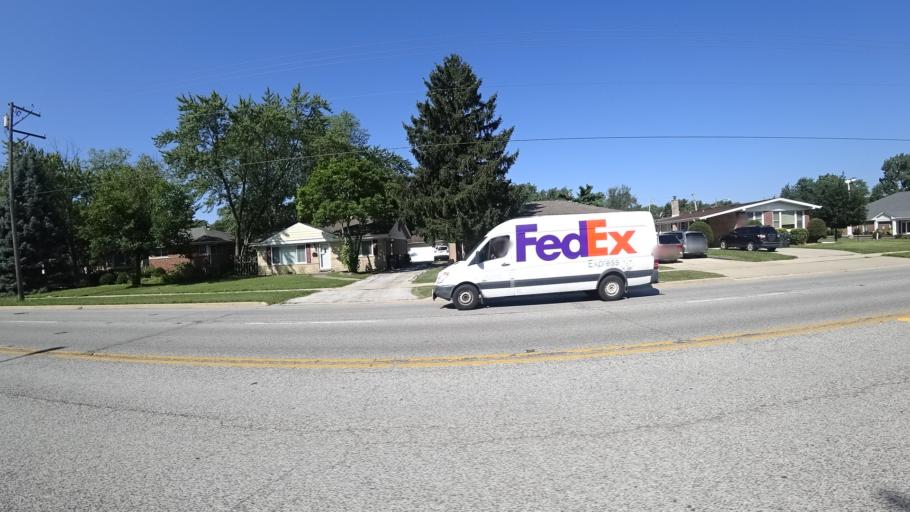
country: US
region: Illinois
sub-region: Cook County
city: Tinley Park
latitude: 41.5763
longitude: -87.7933
